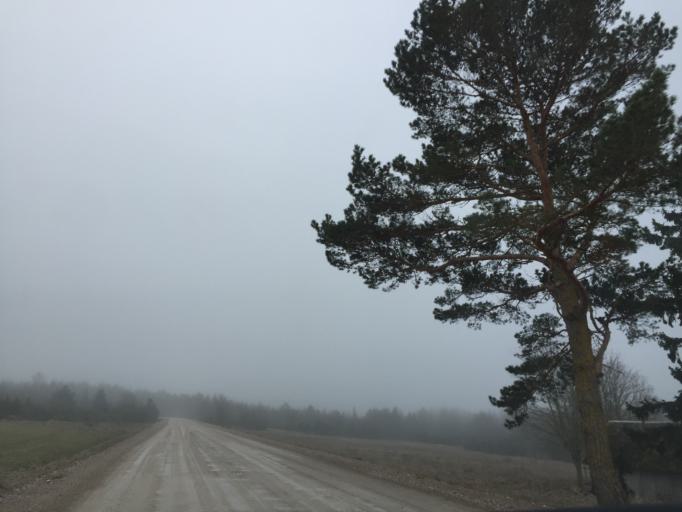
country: EE
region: Saare
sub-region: Kuressaare linn
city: Kuressaare
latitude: 58.4923
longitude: 21.9849
